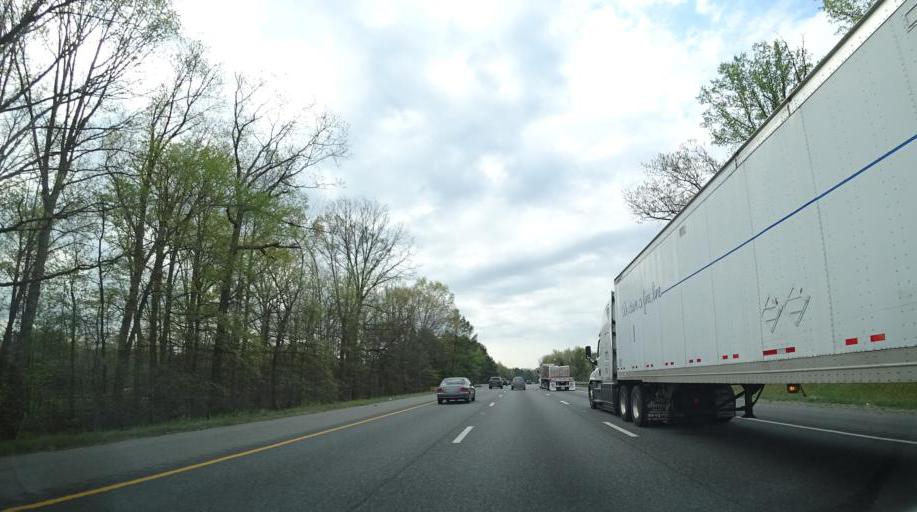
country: US
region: Virginia
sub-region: Hanover County
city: Ashland
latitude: 37.9260
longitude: -77.4638
